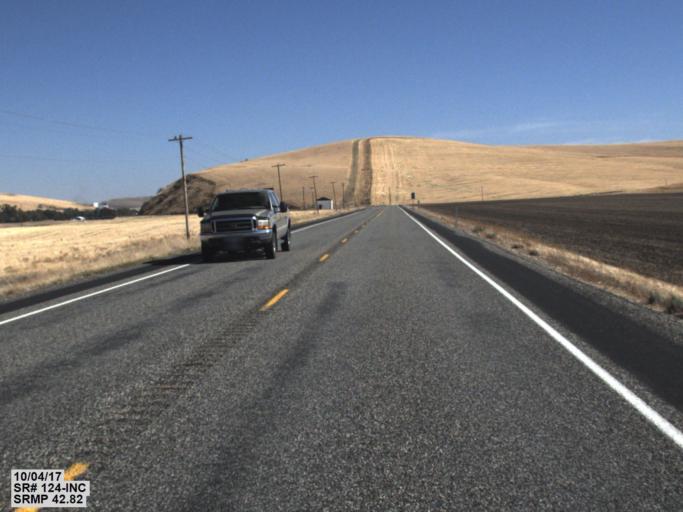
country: US
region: Washington
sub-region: Walla Walla County
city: Waitsburg
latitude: 46.2665
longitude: -118.1960
